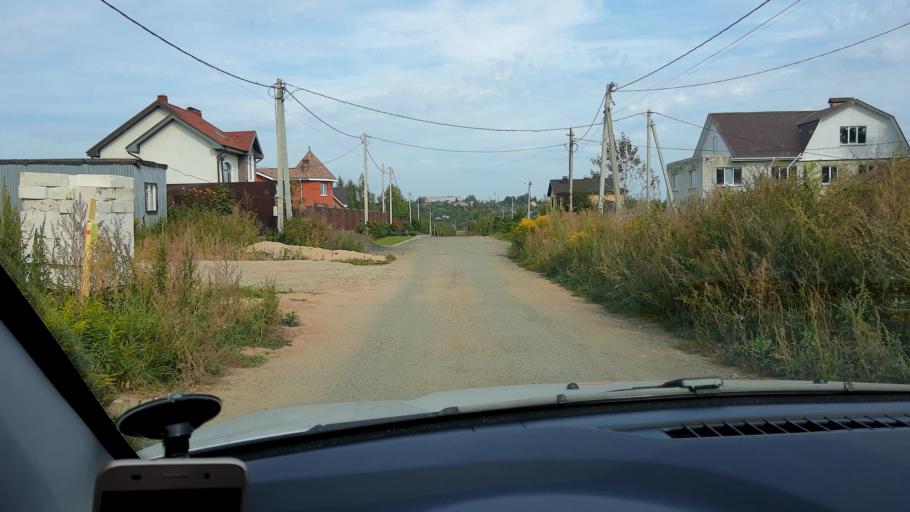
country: RU
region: Nizjnij Novgorod
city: Afonino
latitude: 56.2627
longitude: 44.0664
